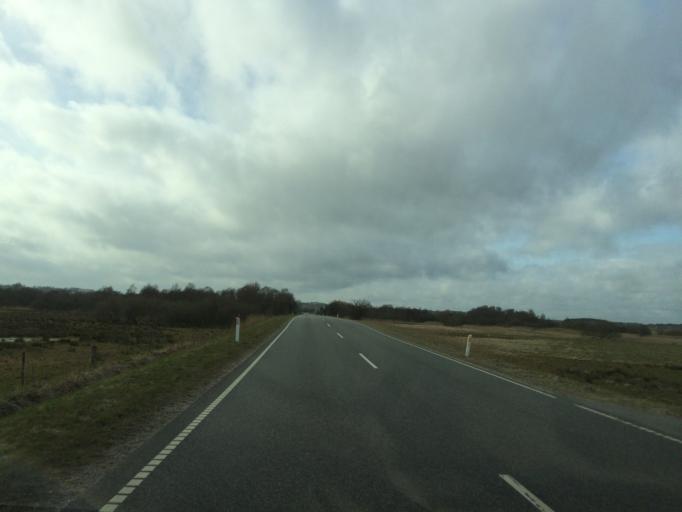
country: DK
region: Central Jutland
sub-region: Randers Kommune
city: Langa
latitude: 56.4877
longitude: 9.8635
